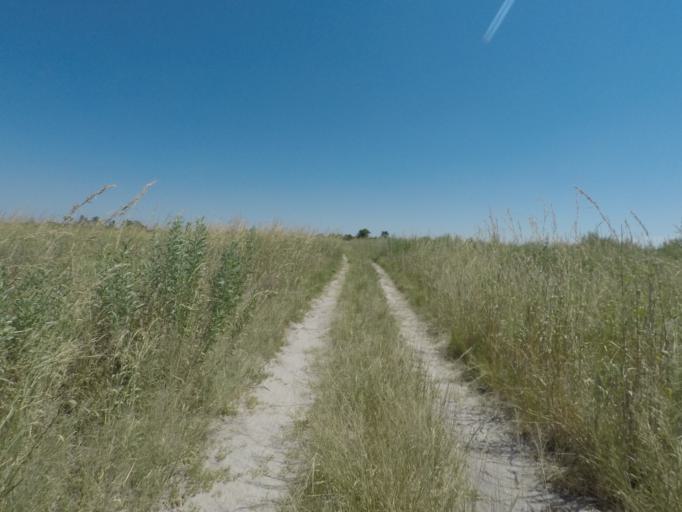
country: BW
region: North West
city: Maun
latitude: -19.4854
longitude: 23.5300
